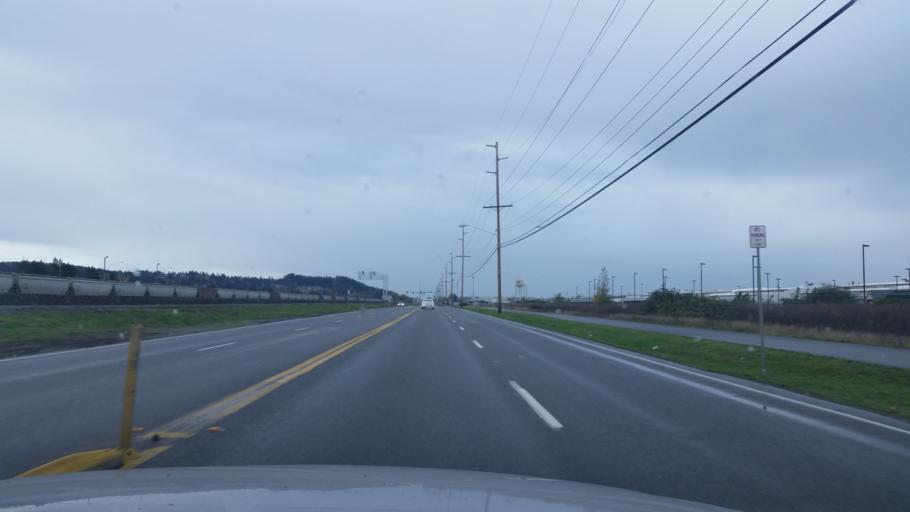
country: US
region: Washington
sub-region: King County
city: Auburn
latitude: 47.2936
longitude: -122.2320
